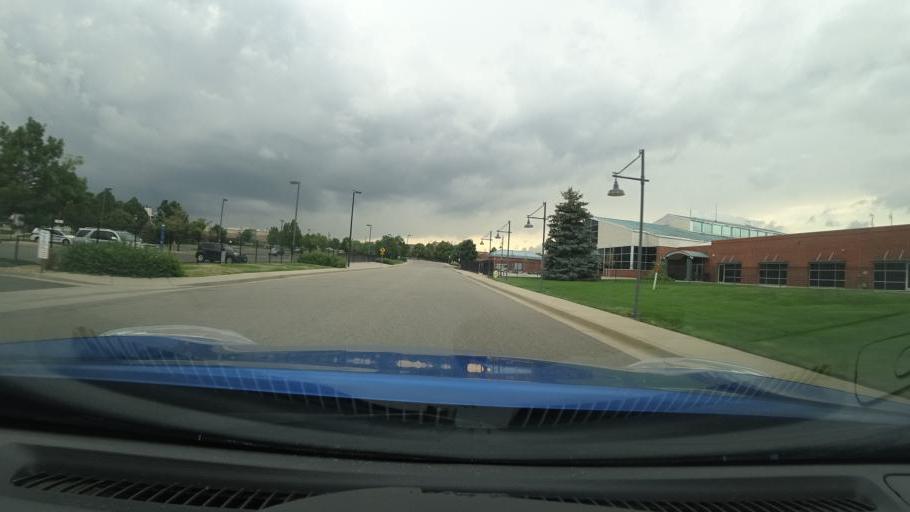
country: US
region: Colorado
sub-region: Adams County
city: Aurora
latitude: 39.7020
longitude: -104.8224
